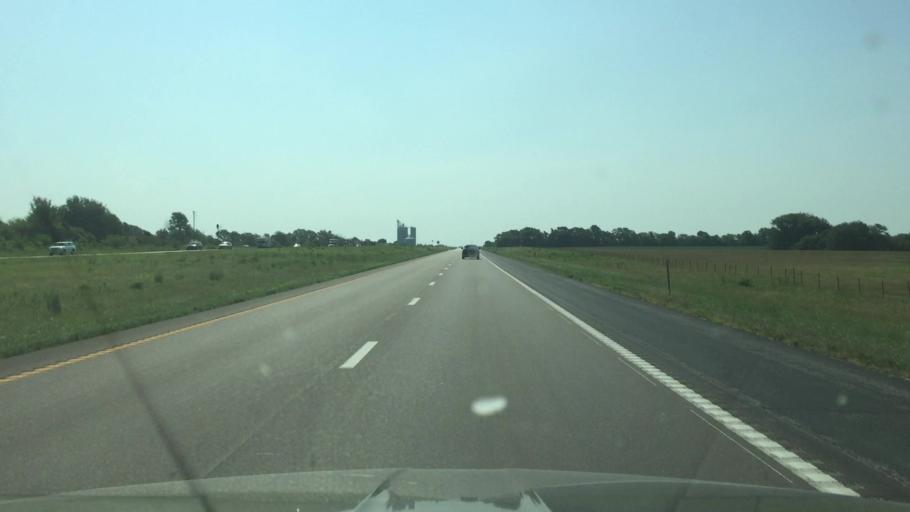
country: US
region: Missouri
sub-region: Pettis County
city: La Monte
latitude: 38.7576
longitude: -93.3674
